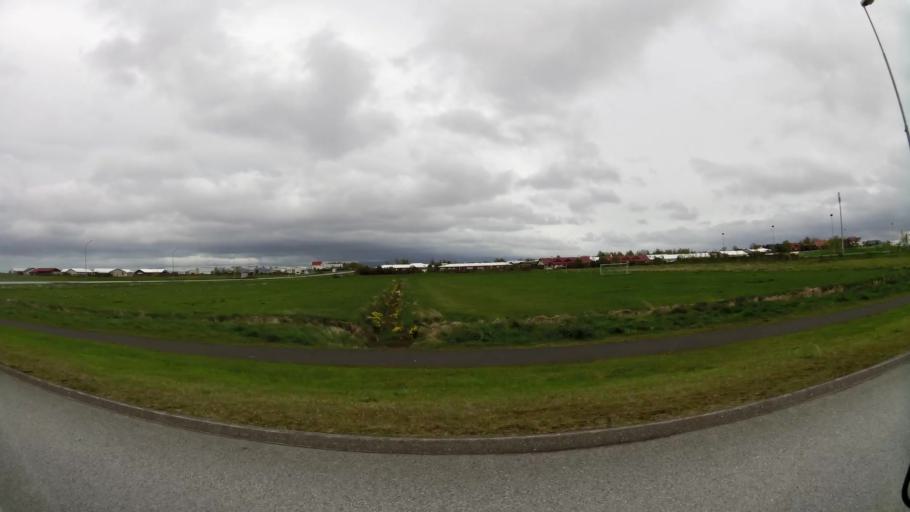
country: IS
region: Capital Region
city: Alftanes
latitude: 64.1059
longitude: -22.0247
